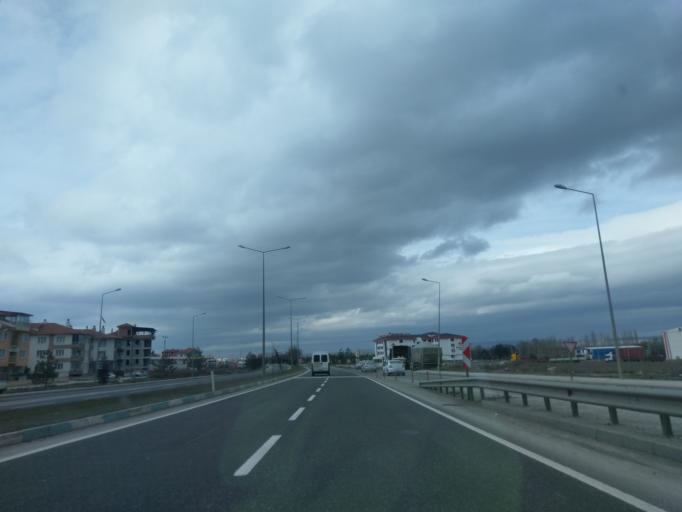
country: TR
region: Kuetahya
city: Kutahya
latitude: 39.4073
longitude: 30.0262
